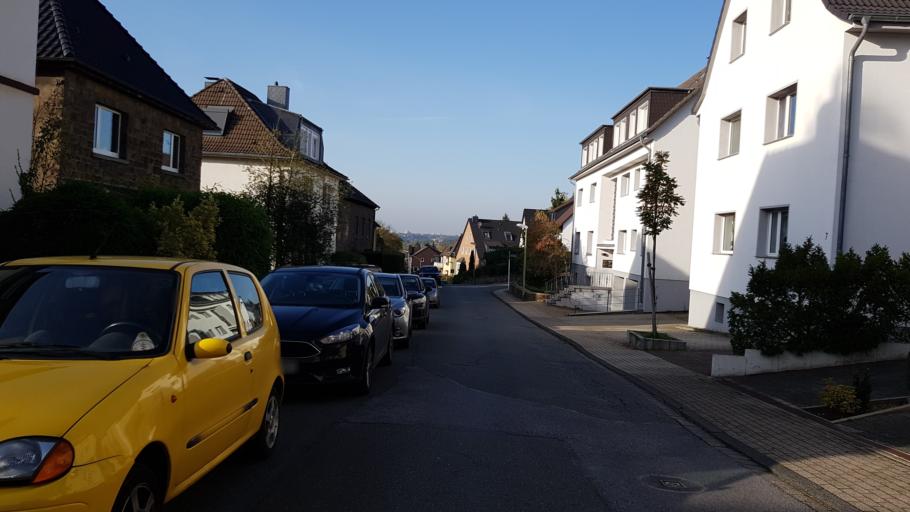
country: DE
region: North Rhine-Westphalia
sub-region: Regierungsbezirk Dusseldorf
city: Velbert
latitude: 51.3929
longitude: 7.0895
